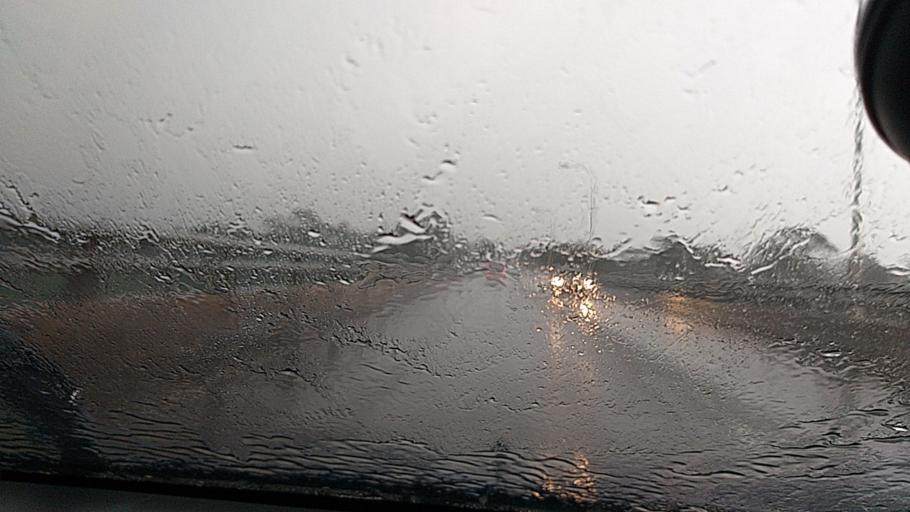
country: AU
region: New South Wales
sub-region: Camden
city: Camden South
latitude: -34.0697
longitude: 150.7036
